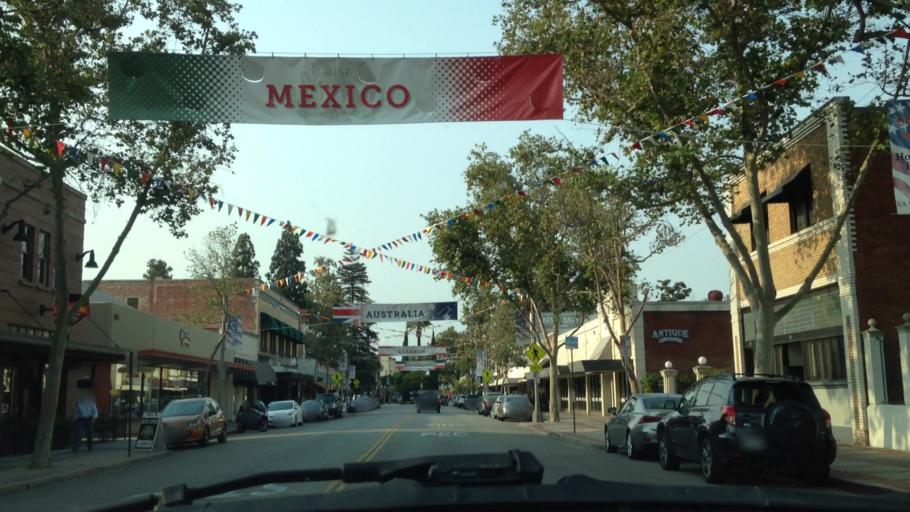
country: US
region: California
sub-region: Orange County
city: Orange
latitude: 33.7860
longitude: -117.8531
